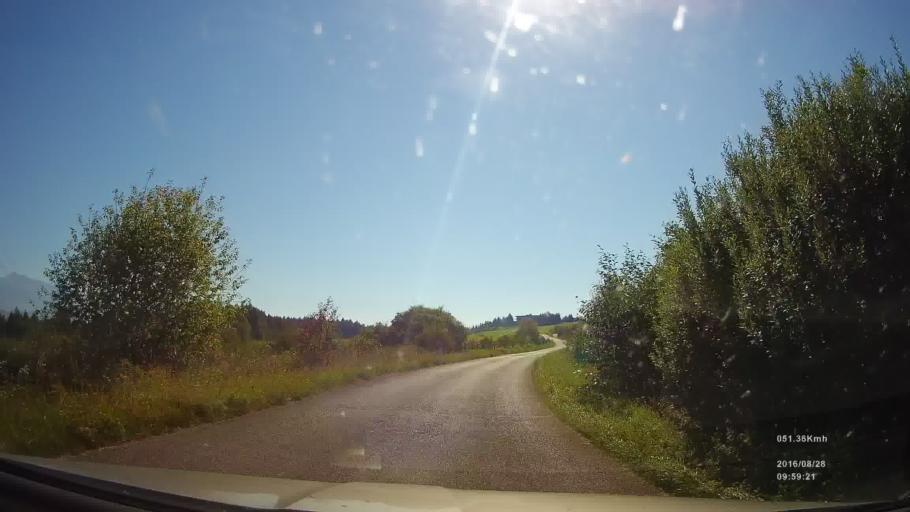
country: SK
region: Zilinsky
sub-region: Okres Liptovsky Mikulas
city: Liptovsky Mikulas
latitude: 49.1133
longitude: 19.4833
